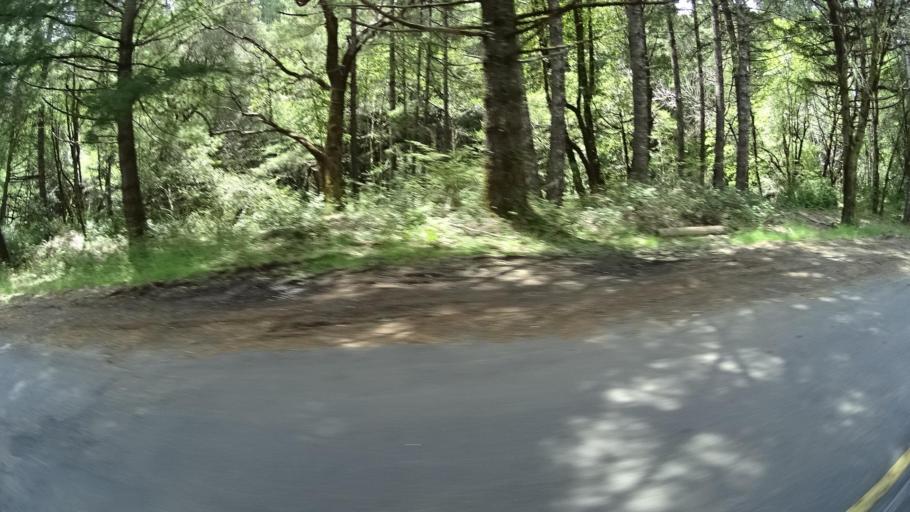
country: US
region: California
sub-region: Humboldt County
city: Redway
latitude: 40.0615
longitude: -123.9614
